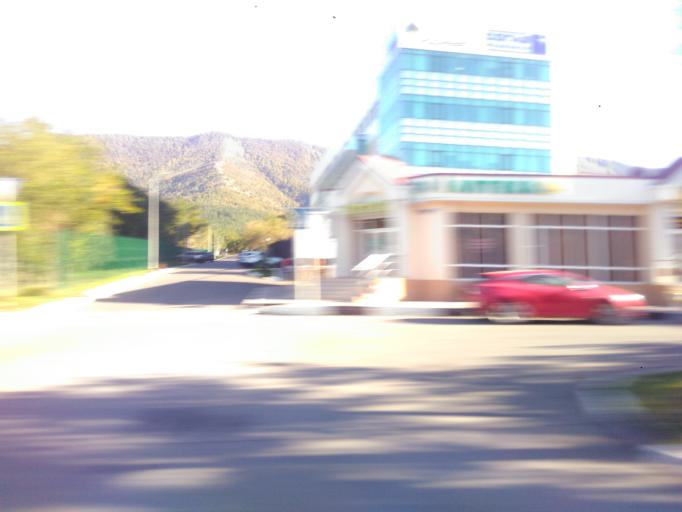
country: RU
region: Krasnodarskiy
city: Gelendzhik
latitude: 44.5811
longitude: 38.0651
